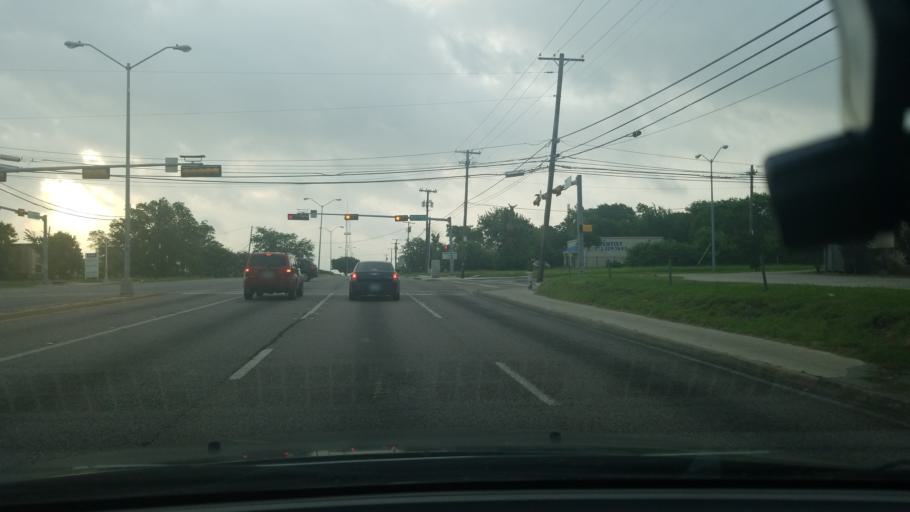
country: US
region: Texas
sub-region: Dallas County
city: Balch Springs
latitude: 32.7622
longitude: -96.6487
